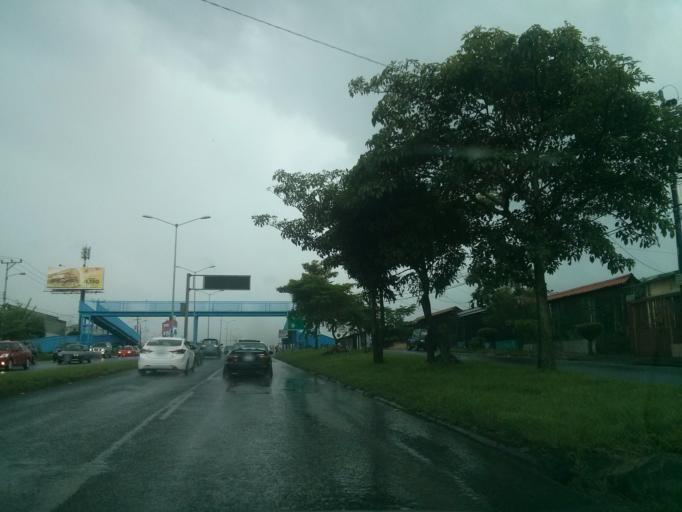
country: CR
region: San Jose
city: San Felipe
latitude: 9.9125
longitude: -84.1036
